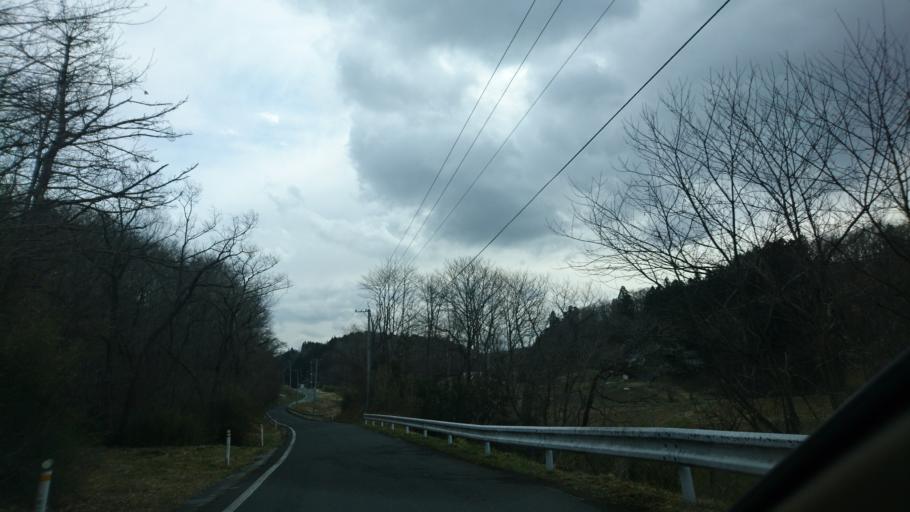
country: JP
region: Iwate
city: Ichinoseki
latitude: 38.8954
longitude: 141.1699
